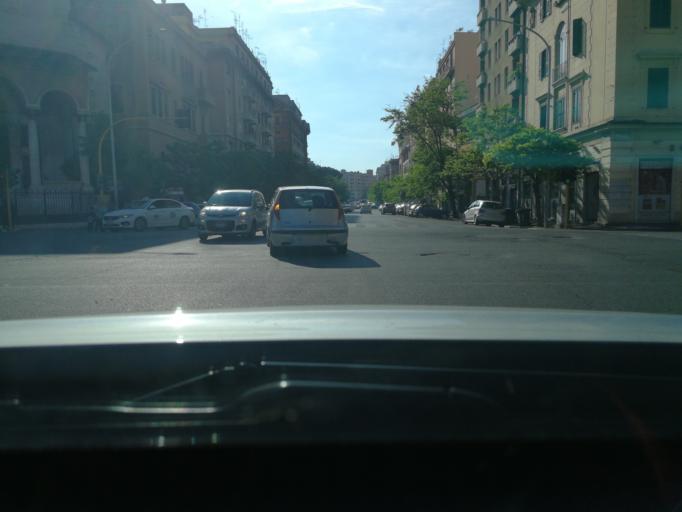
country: IT
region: Latium
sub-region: Citta metropolitana di Roma Capitale
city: Rome
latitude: 41.8846
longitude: 12.5147
